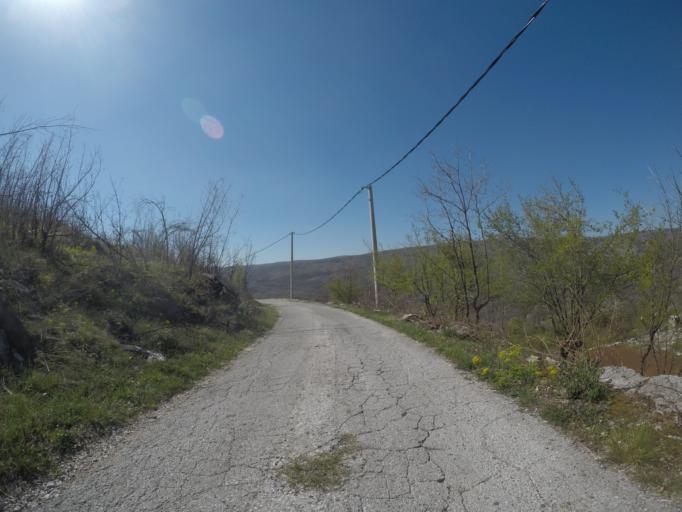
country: ME
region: Danilovgrad
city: Danilovgrad
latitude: 42.5311
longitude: 19.0242
